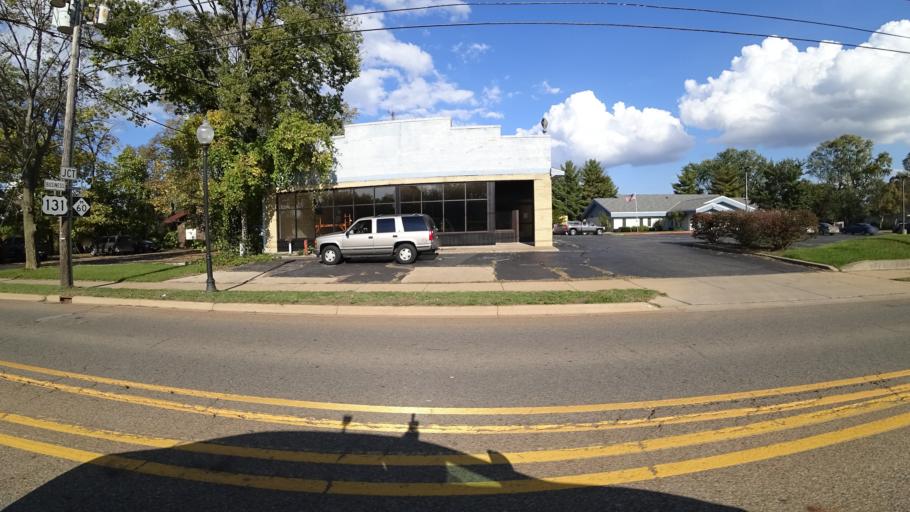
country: US
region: Michigan
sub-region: Saint Joseph County
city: Three Rivers
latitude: 41.9426
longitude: -85.6316
